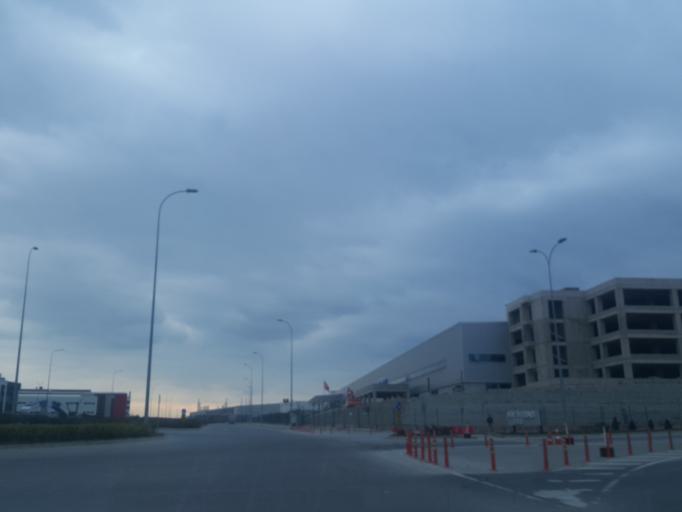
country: TR
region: Kocaeli
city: Hereke
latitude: 40.8380
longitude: 29.5774
